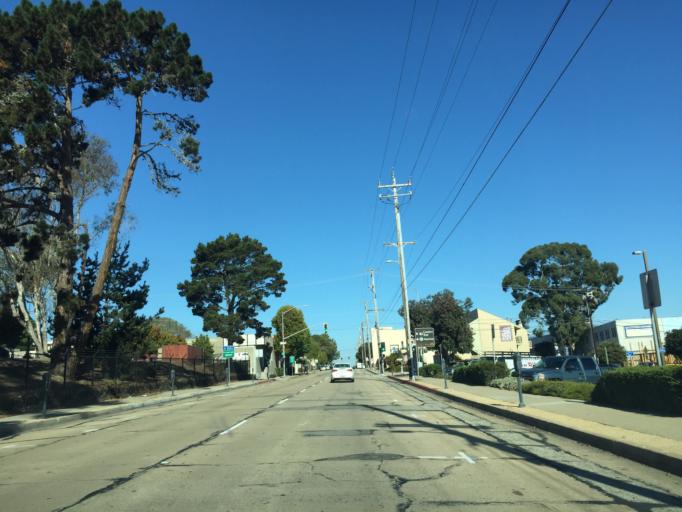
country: US
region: California
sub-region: Monterey County
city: Monterey
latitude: 36.6096
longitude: -121.8971
